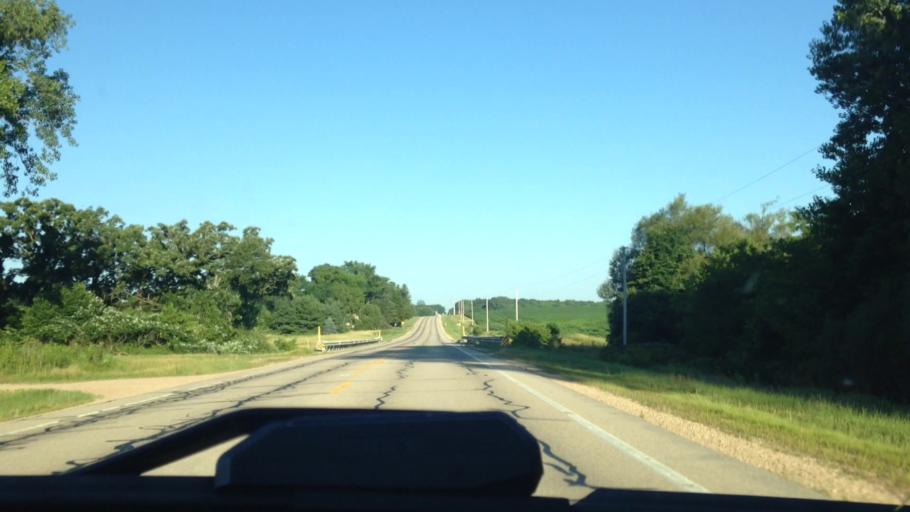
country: US
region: Wisconsin
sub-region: Columbia County
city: Fall River
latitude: 43.3407
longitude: -89.1259
